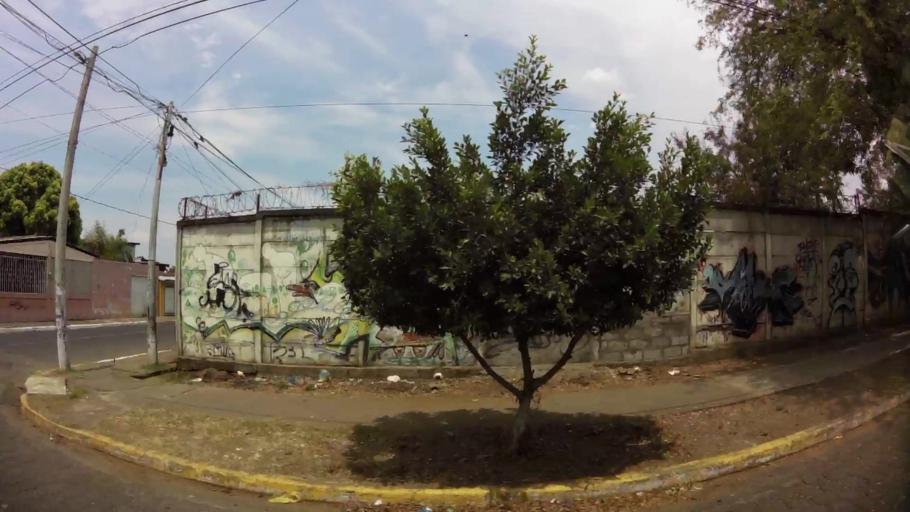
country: NI
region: Managua
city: Ciudad Sandino
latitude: 12.1526
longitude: -86.2999
